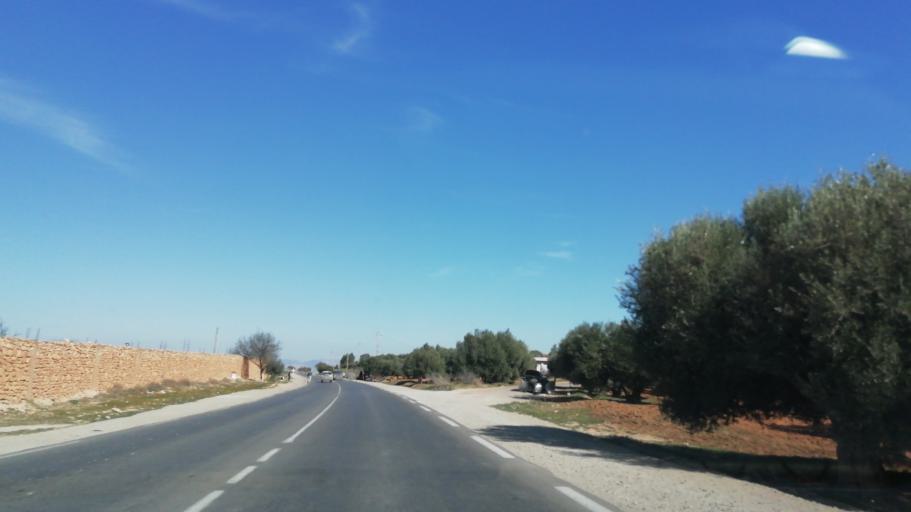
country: DZ
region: Mascara
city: Oued el Abtal
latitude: 35.4278
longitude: 0.4713
